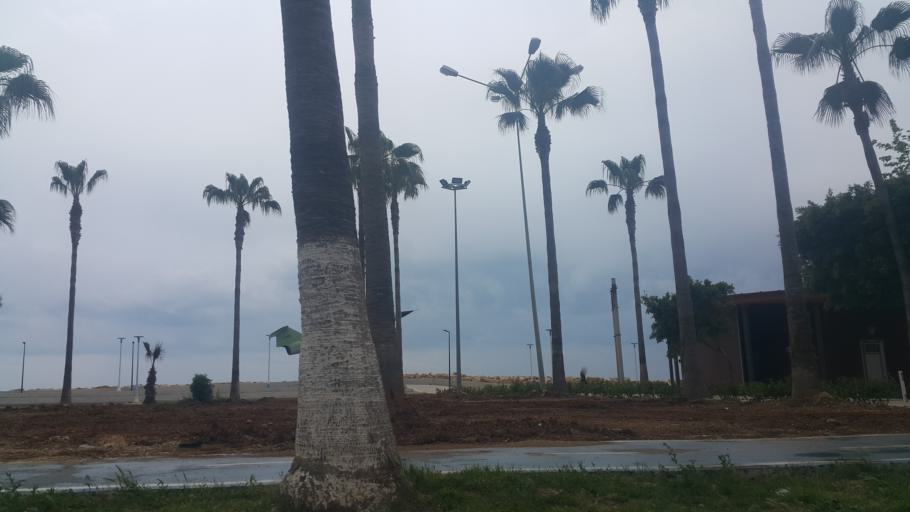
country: TR
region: Mersin
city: Mercin
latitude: 36.7802
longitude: 34.5987
